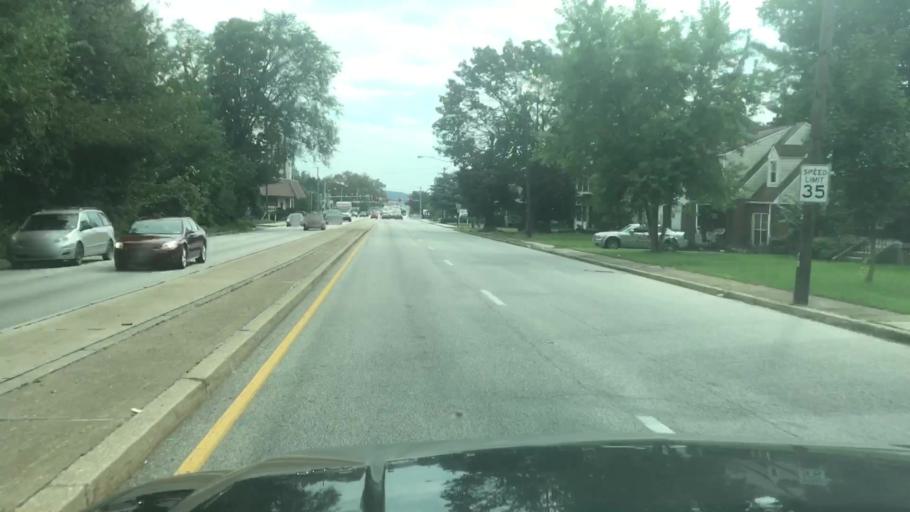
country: US
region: Pennsylvania
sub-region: Cumberland County
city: Camp Hill
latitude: 40.2420
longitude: -76.9352
